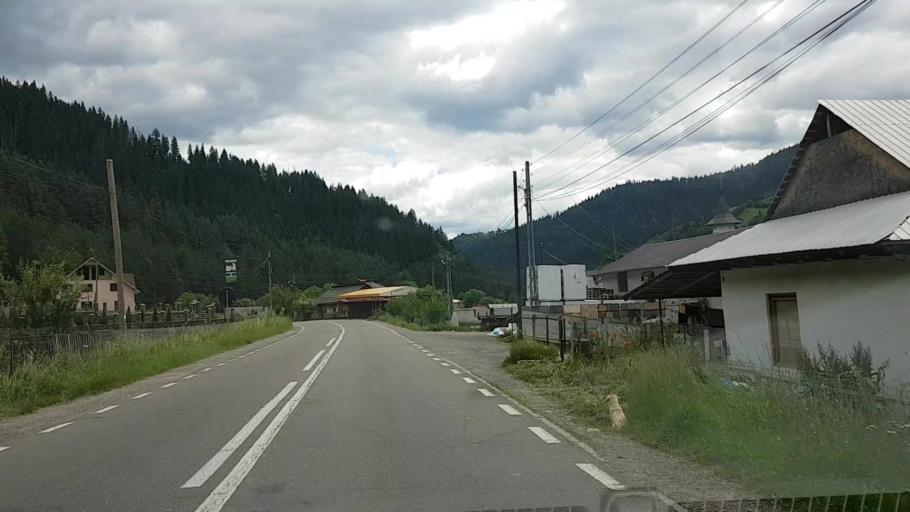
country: RO
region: Neamt
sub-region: Comuna Poiana Teiului
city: Poiana Teiului
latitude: 47.1286
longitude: 25.9027
